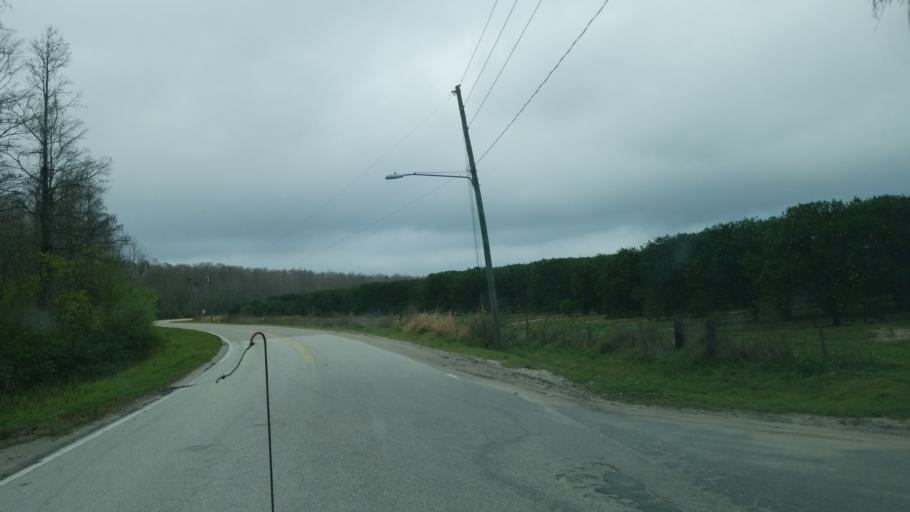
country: US
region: Florida
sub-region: Lake County
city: Four Corners
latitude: 28.2576
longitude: -81.7050
